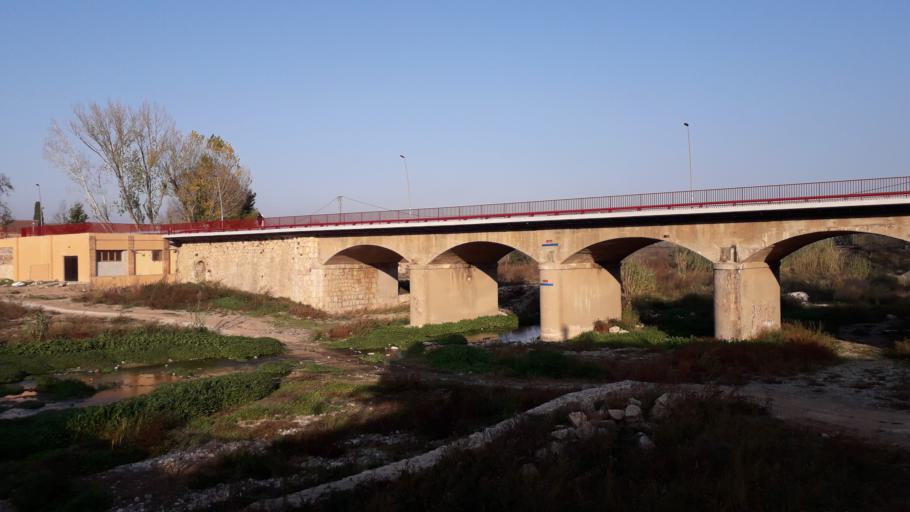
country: ES
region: Catalonia
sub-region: Provincia de Tarragona
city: Montblanc
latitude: 41.3801
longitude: 1.1613
